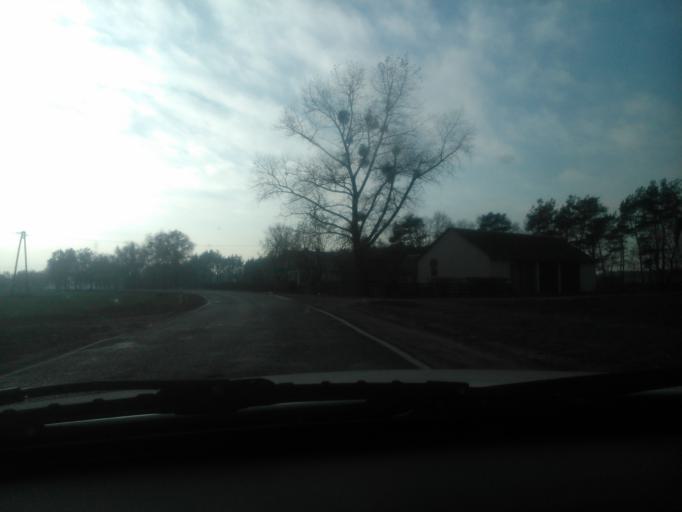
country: PL
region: Masovian Voivodeship
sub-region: Powiat ostrolecki
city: Czarnia
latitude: 53.3244
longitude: 21.1395
